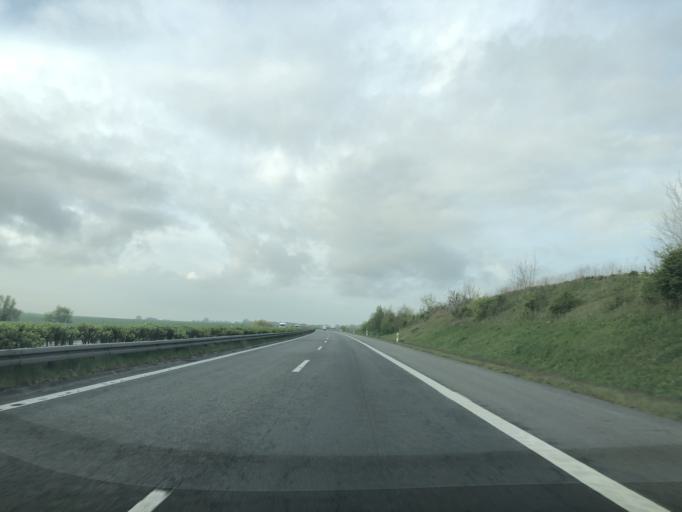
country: DE
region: Mecklenburg-Vorpommern
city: Bad Sulze
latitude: 54.0420
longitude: 12.6102
